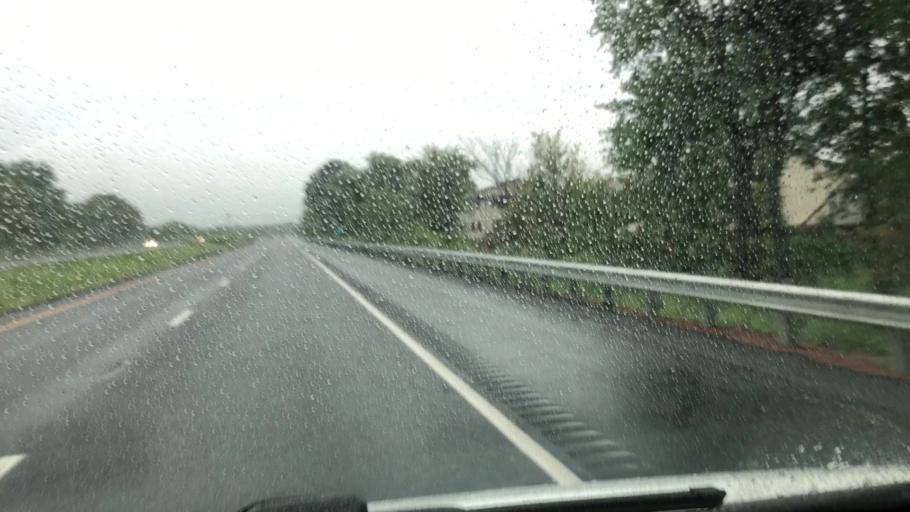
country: US
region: Massachusetts
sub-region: Hampshire County
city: Northampton
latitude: 42.3379
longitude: -72.6307
